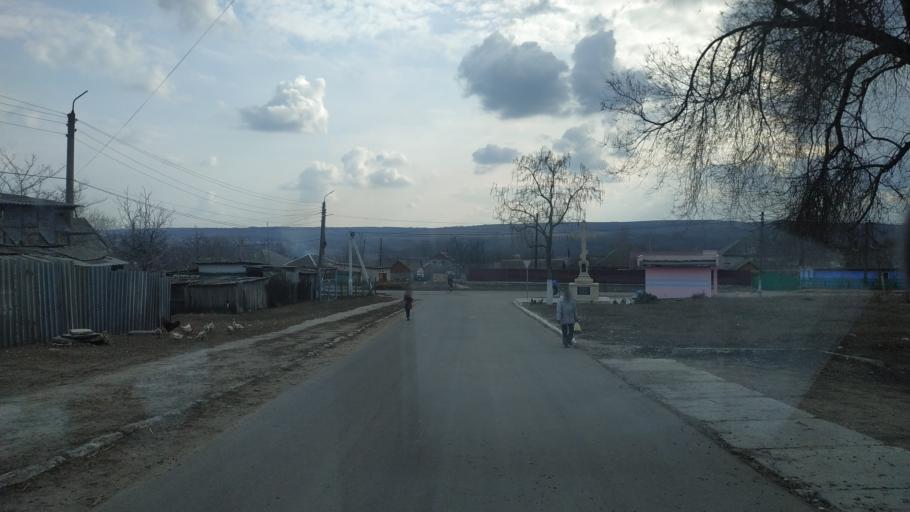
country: MD
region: Anenii Noi
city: Anenii Noi
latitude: 46.8901
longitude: 29.2830
